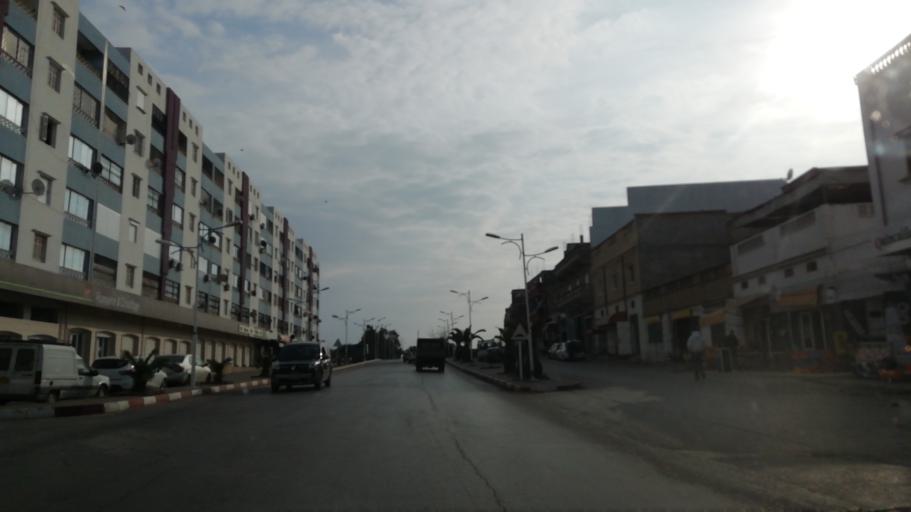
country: DZ
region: Mostaganem
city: Mostaganem
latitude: 35.8928
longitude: 0.0761
